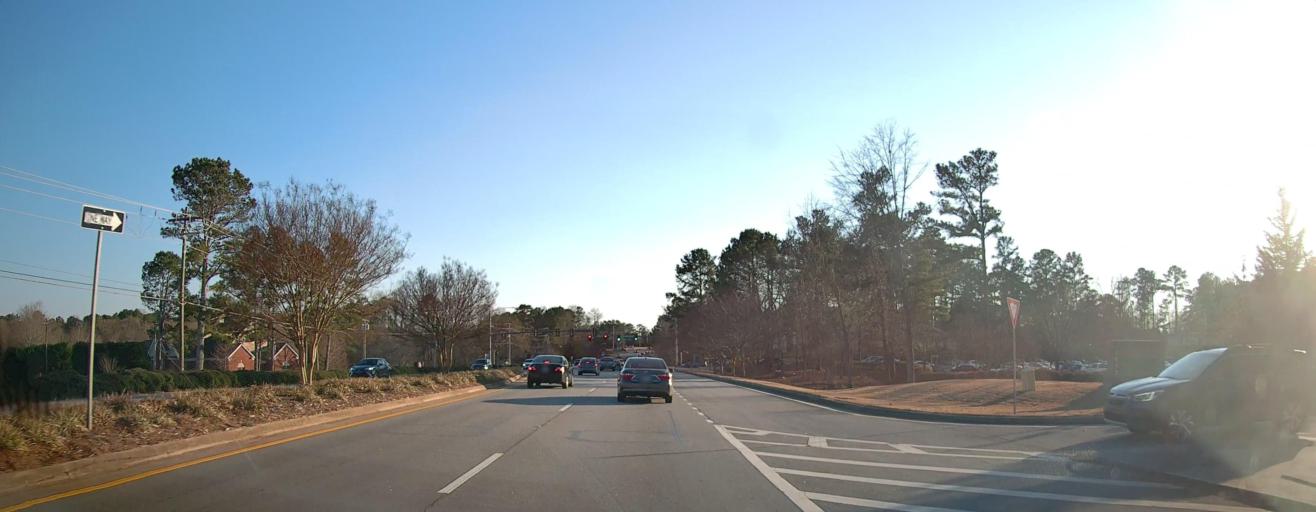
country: US
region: Georgia
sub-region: Fayette County
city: Peachtree City
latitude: 33.4202
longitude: -84.5590
